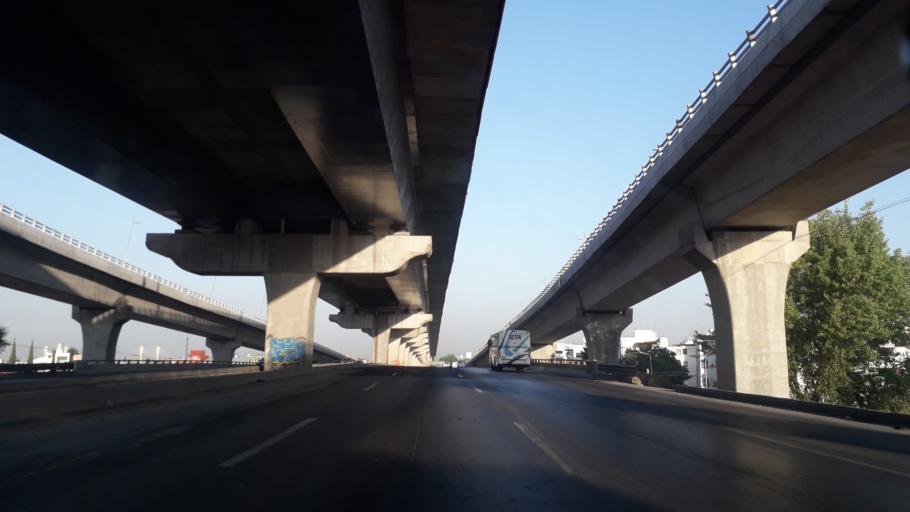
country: MX
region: Puebla
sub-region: Puebla
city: San Sebastian de Aparicio
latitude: 19.0827
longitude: -98.1796
